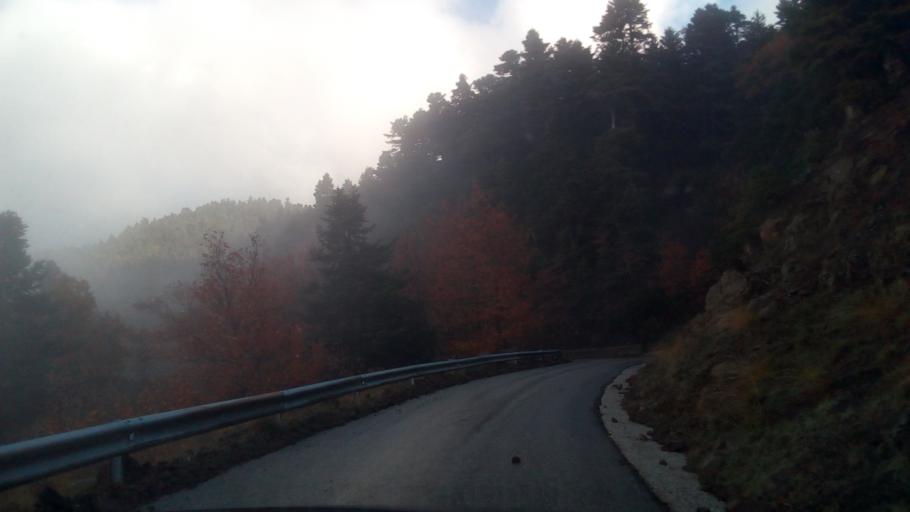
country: GR
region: West Greece
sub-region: Nomos Aitolias kai Akarnanias
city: Nafpaktos
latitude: 38.5594
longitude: 21.9287
